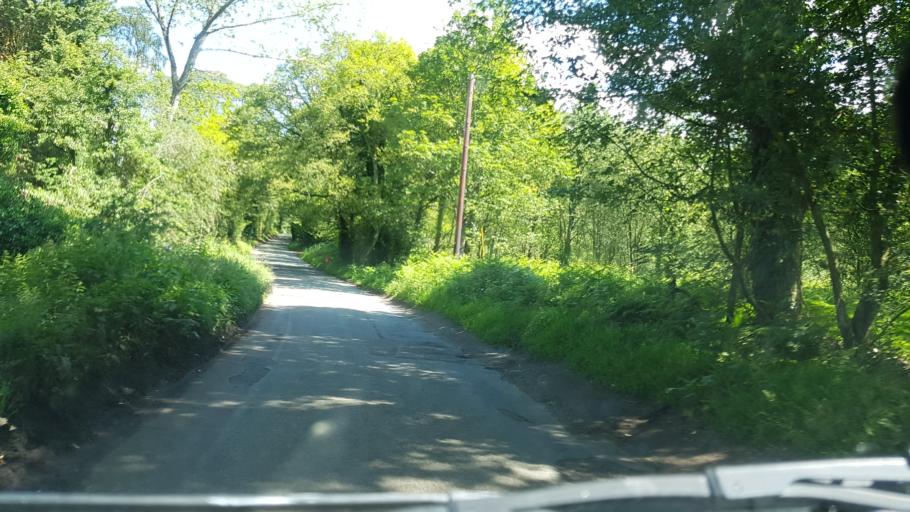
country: GB
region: England
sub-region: Worcestershire
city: Kidderminster
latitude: 52.4400
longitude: -2.2588
